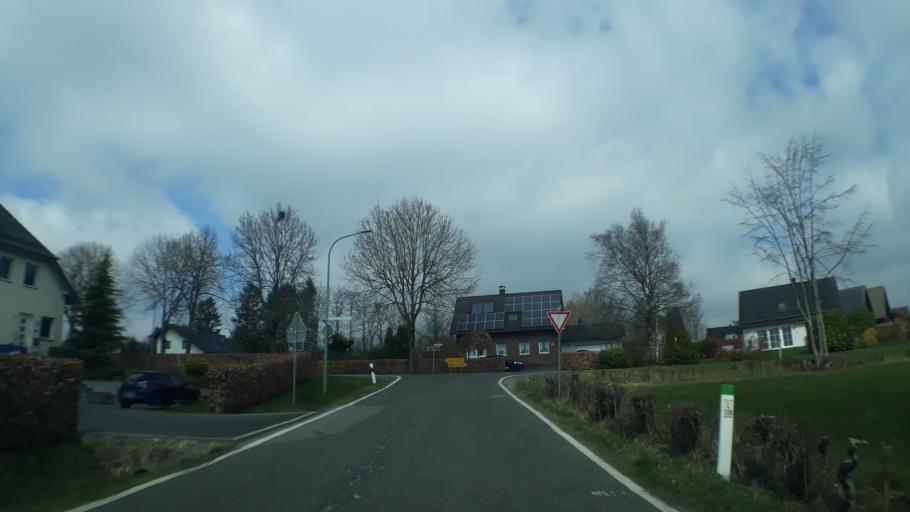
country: DE
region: North Rhine-Westphalia
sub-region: Regierungsbezirk Koln
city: Monschau
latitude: 50.5636
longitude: 6.2109
